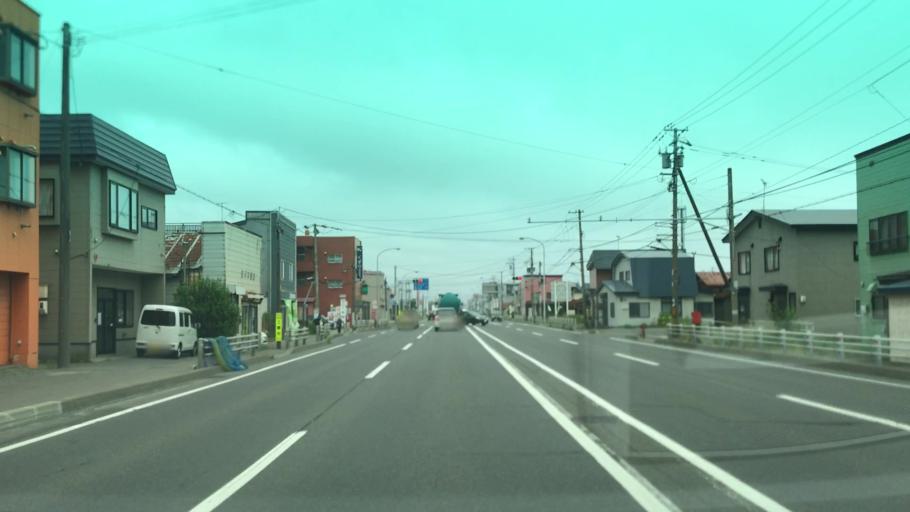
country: JP
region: Hokkaido
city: Muroran
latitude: 42.3560
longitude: 141.0495
